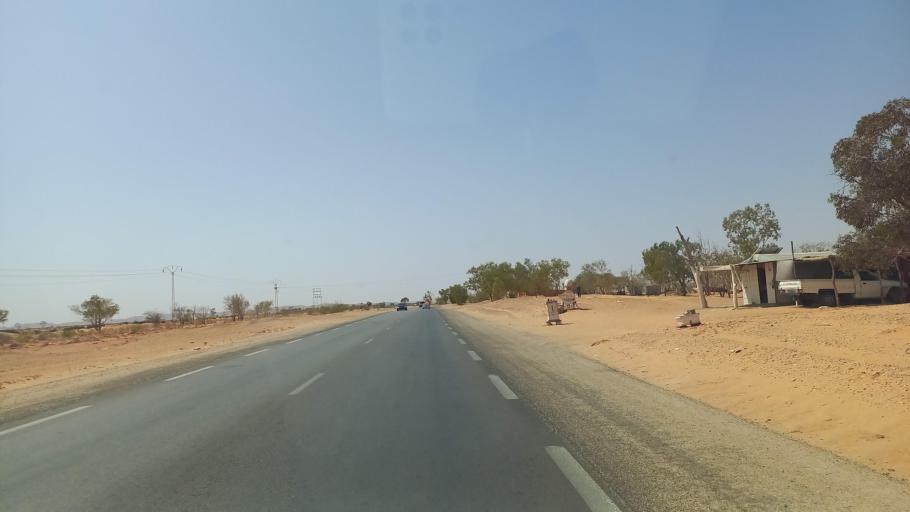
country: TN
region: Madanin
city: Medenine
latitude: 33.2130
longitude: 10.4469
